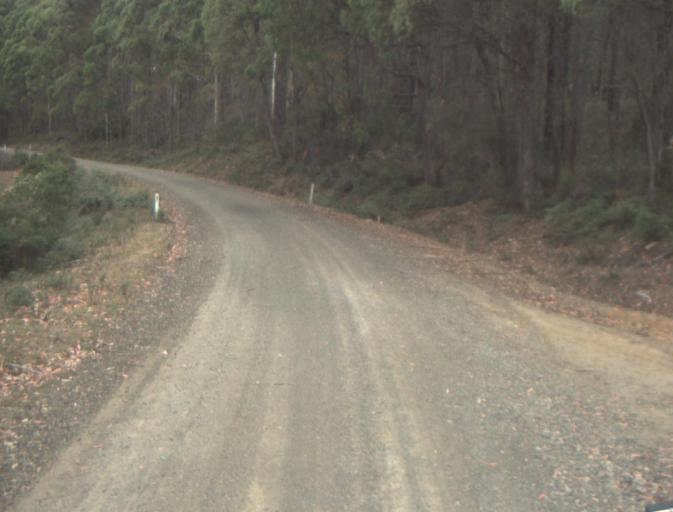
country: AU
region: Tasmania
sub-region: Dorset
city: Scottsdale
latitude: -41.4102
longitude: 147.5167
